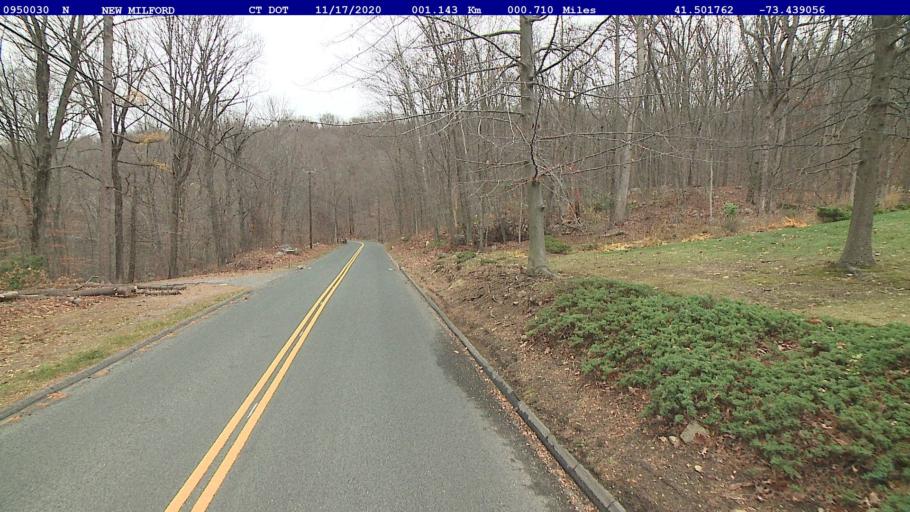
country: US
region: Connecticut
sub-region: Litchfield County
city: New Milford
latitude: 41.5018
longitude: -73.4390
